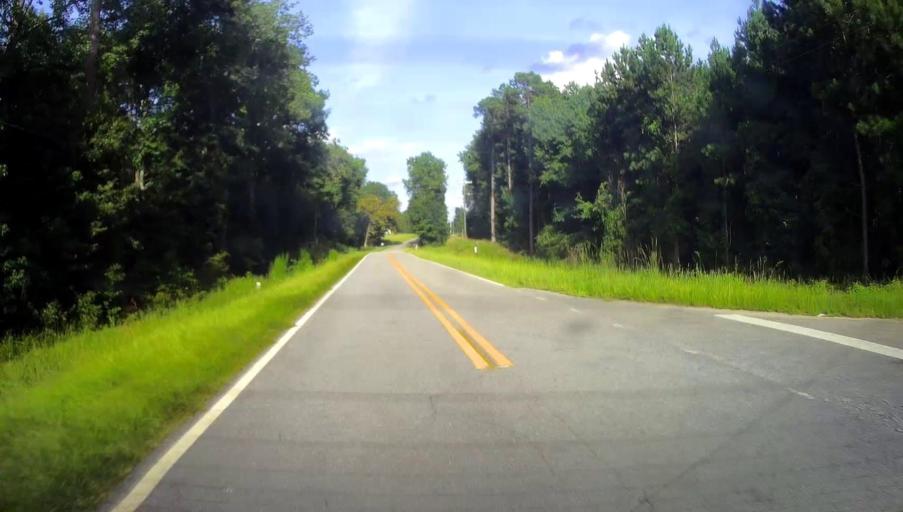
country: US
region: Georgia
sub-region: Crawford County
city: Knoxville
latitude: 32.7560
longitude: -83.9306
